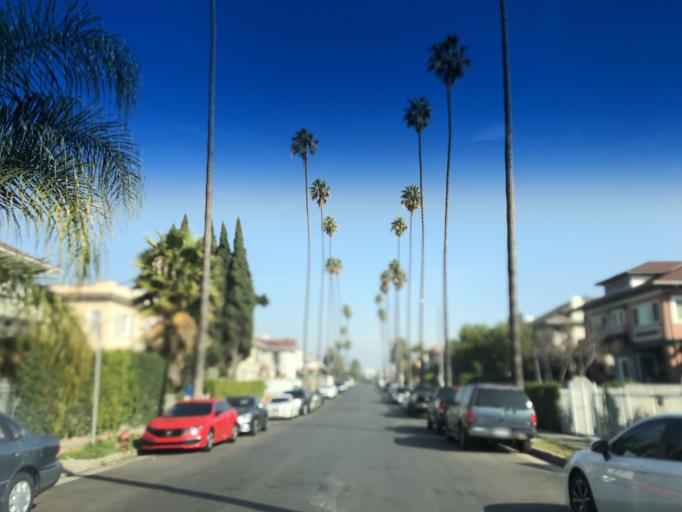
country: US
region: California
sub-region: Los Angeles County
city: Hollywood
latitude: 34.0489
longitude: -118.3205
